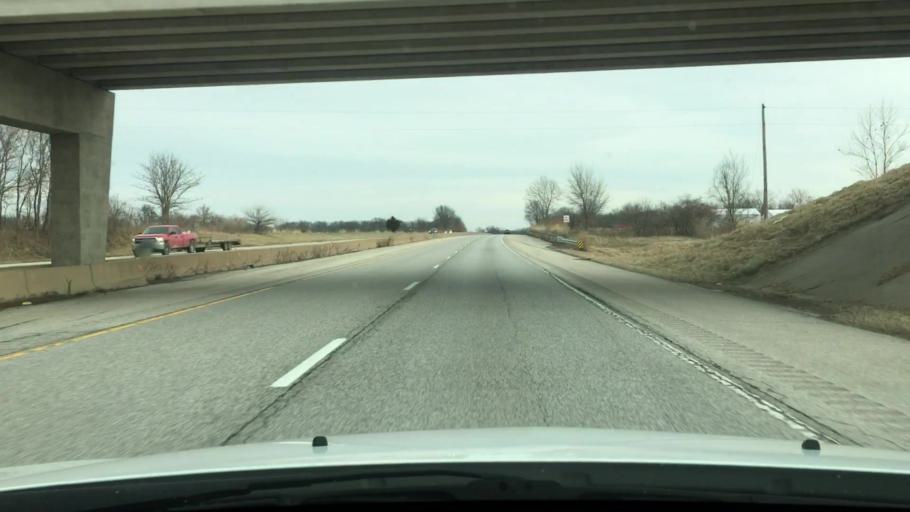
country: US
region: Illinois
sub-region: Pike County
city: Griggsville
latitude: 39.6811
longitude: -90.6718
